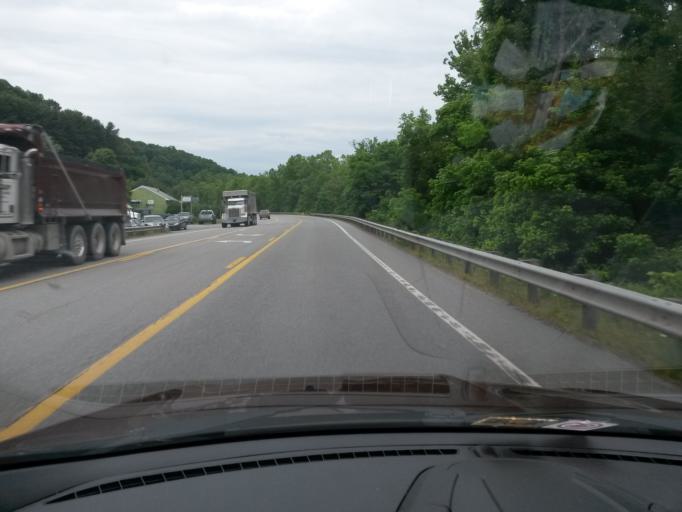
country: US
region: West Virginia
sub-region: Lewis County
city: Weston
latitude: 39.0295
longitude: -80.4350
